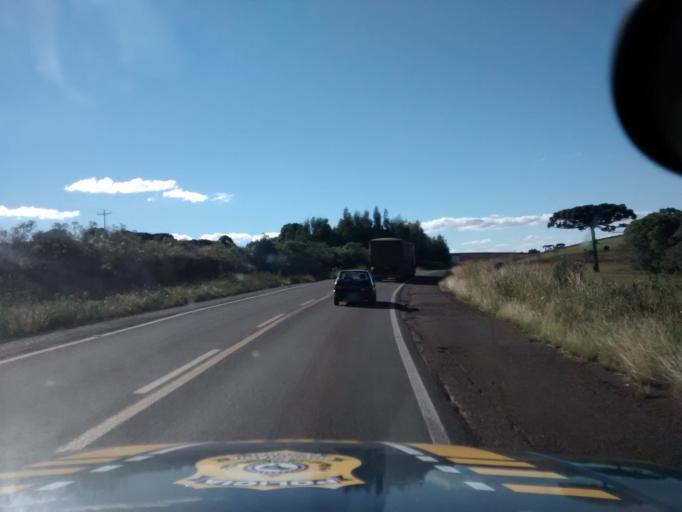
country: BR
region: Rio Grande do Sul
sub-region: Lagoa Vermelha
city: Lagoa Vermelha
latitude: -28.2788
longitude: -51.4678
